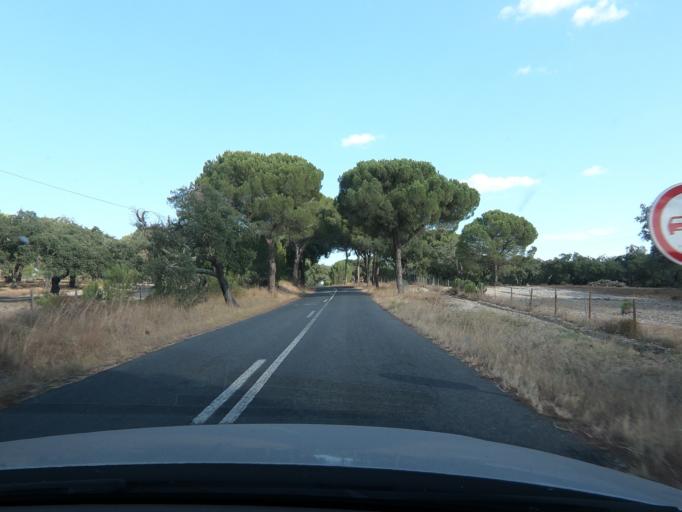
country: PT
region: Setubal
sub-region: Alcacer do Sal
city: Alcacer do Sal
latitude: 38.2639
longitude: -8.3381
